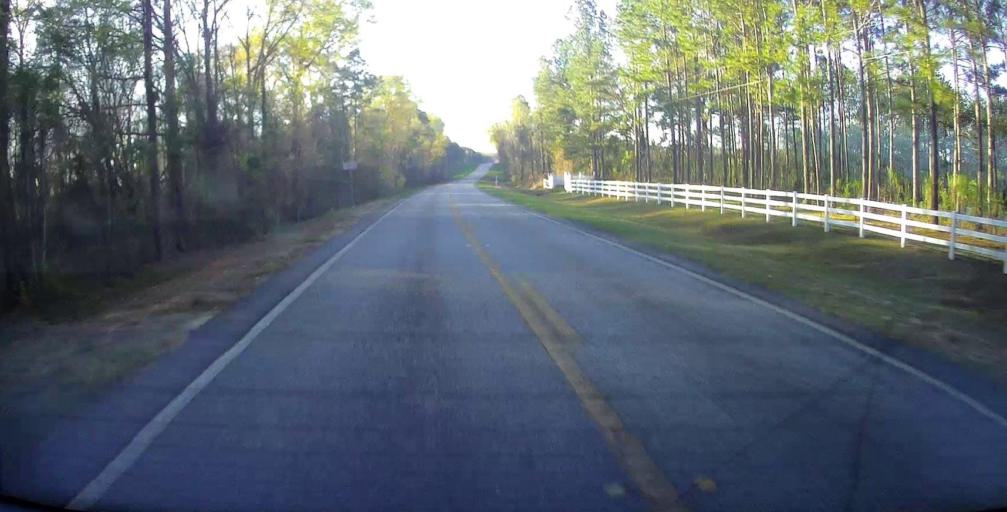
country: US
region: Georgia
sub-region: Wilcox County
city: Abbeville
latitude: 32.1104
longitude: -83.3169
